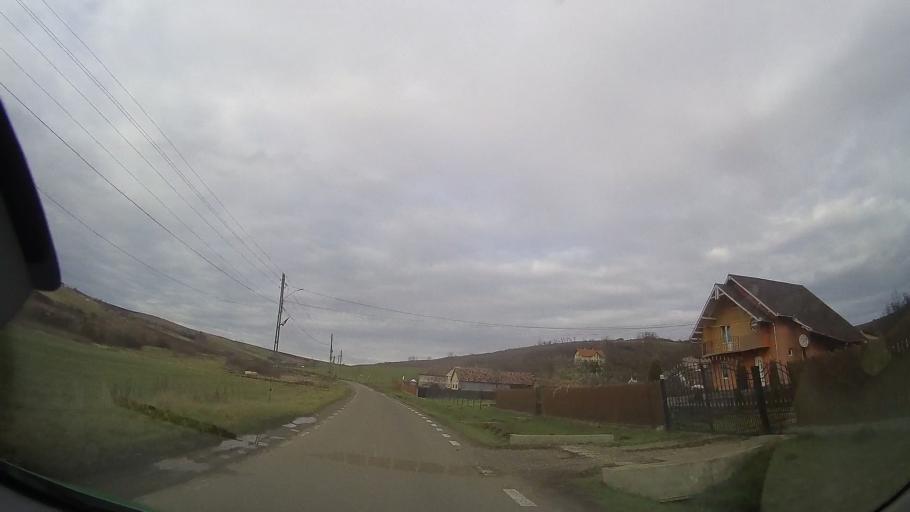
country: RO
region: Mures
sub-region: Comuna Cozma
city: Cozma
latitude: 46.8159
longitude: 24.4942
